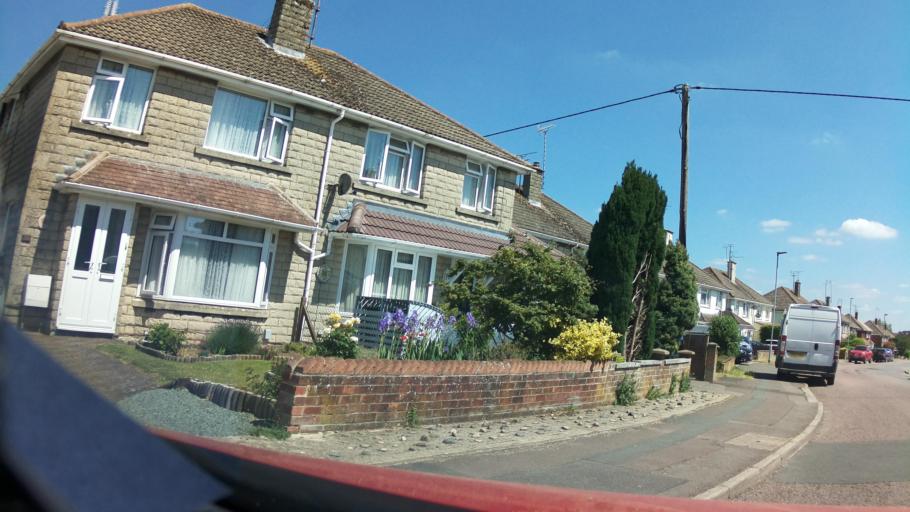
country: GB
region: England
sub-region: Wiltshire
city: Royal Wootton Bassett
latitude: 51.5449
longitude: -1.8935
